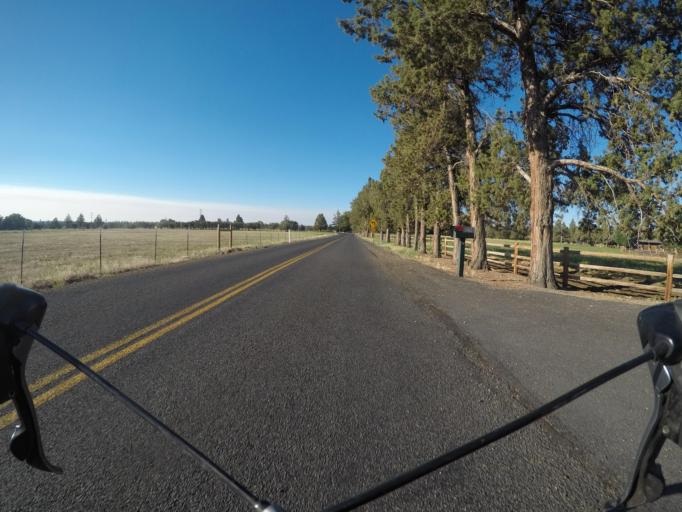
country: US
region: Oregon
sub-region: Deschutes County
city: Redmond
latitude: 44.2638
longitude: -121.2451
